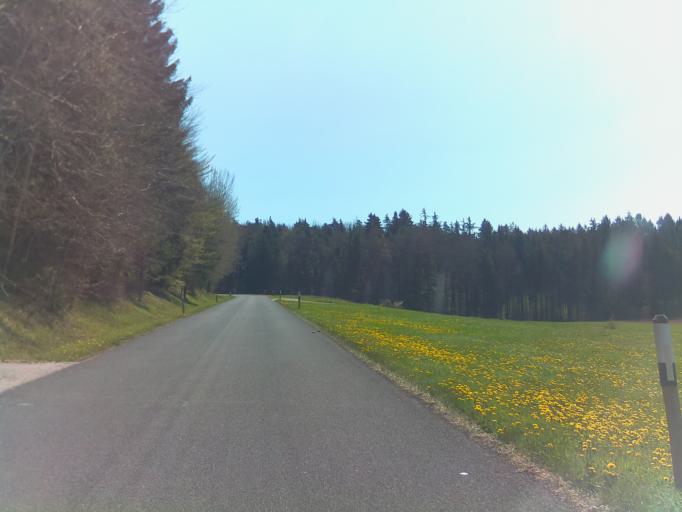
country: DE
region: Bavaria
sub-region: Regierungsbezirk Mittelfranken
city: Alfeld
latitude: 49.4111
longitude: 11.5786
